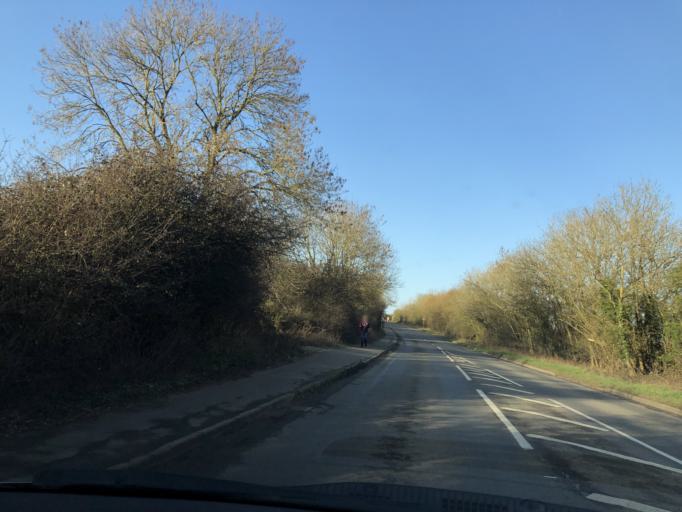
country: GB
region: England
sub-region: Oxfordshire
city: Witney
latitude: 51.7750
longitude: -1.5159
